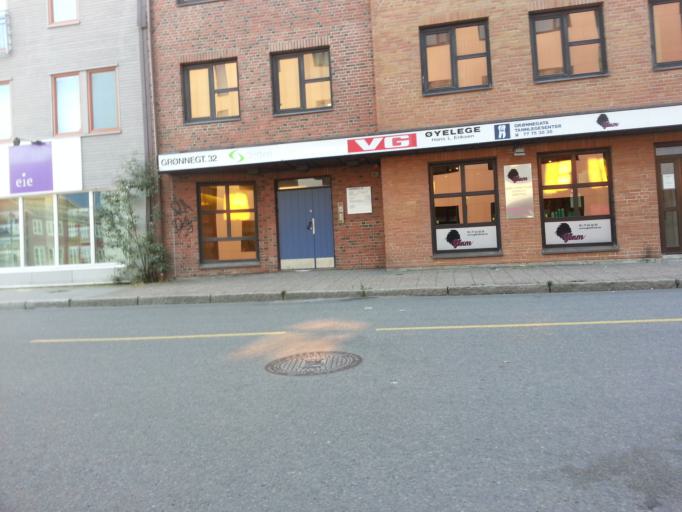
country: NO
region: Troms
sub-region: Tromso
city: Tromso
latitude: 69.6474
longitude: 18.9520
